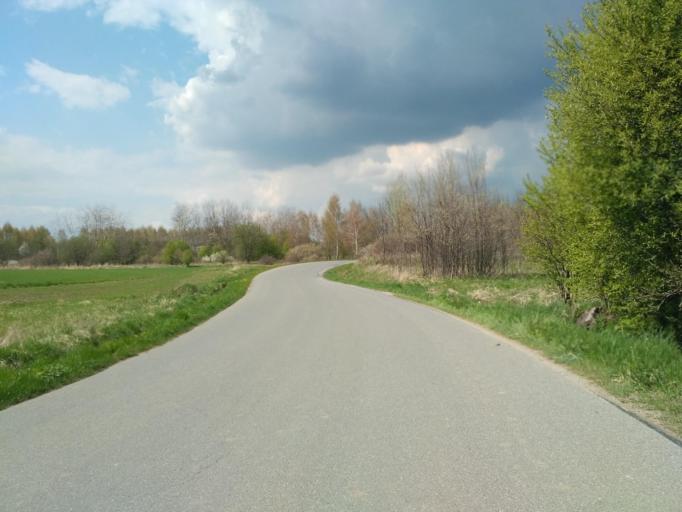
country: PL
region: Subcarpathian Voivodeship
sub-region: Powiat brzozowski
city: Gorki
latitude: 49.6569
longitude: 22.0307
